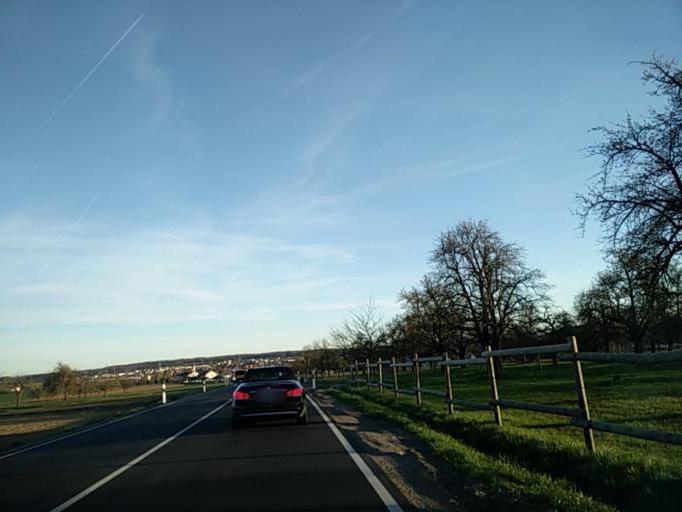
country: DE
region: Baden-Wuerttemberg
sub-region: Regierungsbezirk Stuttgart
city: Holzgerlingen
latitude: 48.6243
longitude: 9.0212
